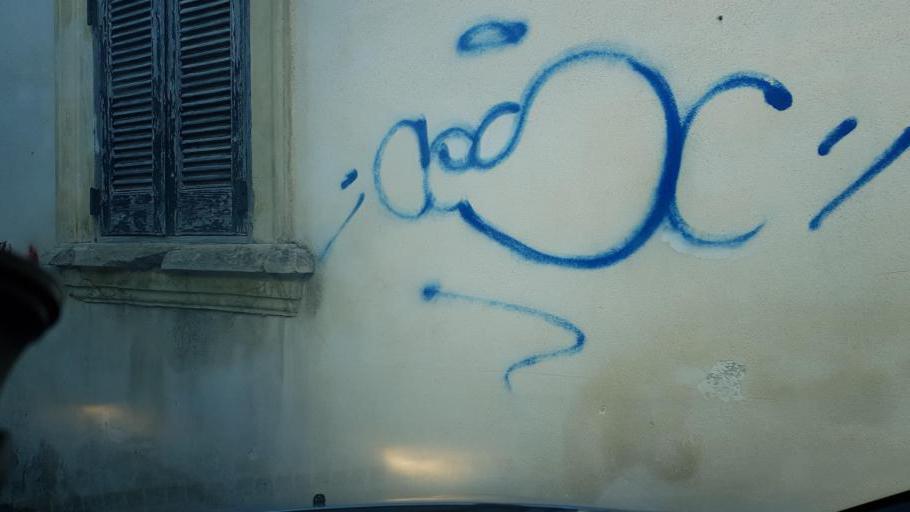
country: IT
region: Apulia
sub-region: Provincia di Lecce
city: Guagnano
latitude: 40.4027
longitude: 17.9521
